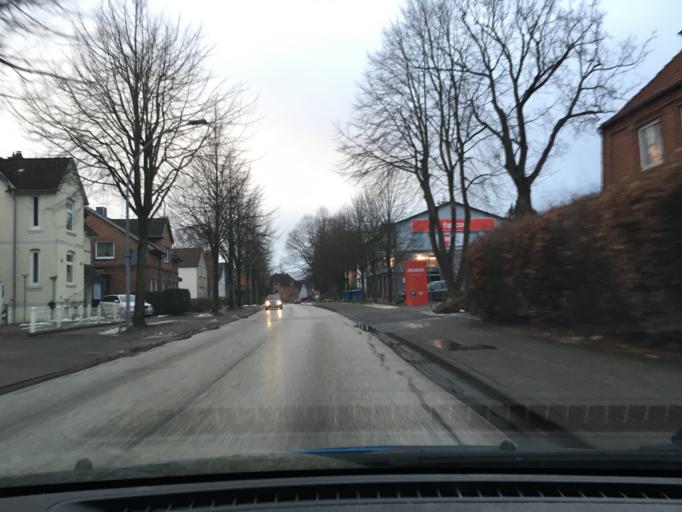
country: DE
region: Schleswig-Holstein
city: Itzehoe
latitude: 53.9361
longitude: 9.5008
